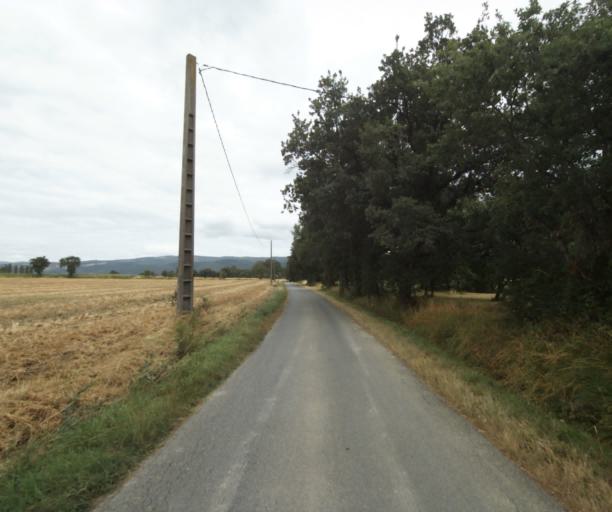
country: FR
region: Midi-Pyrenees
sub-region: Departement du Tarn
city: Soreze
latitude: 43.4812
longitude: 2.0621
